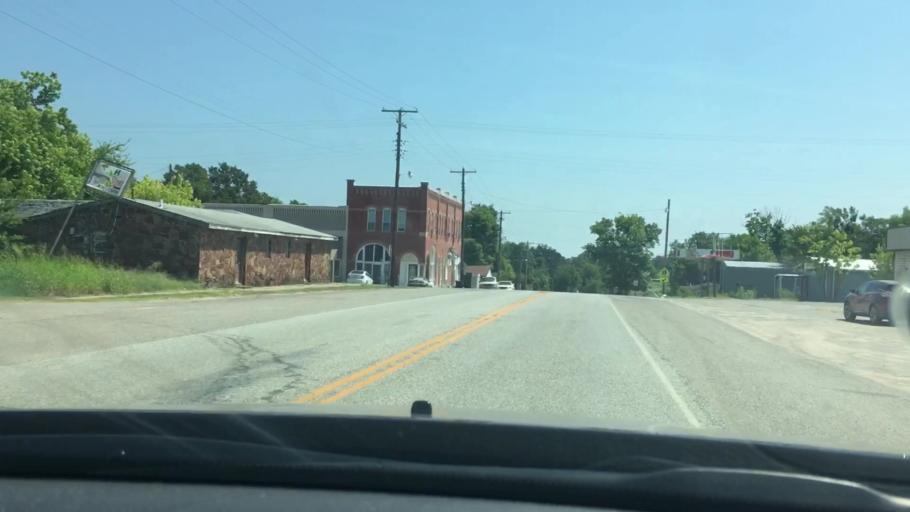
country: US
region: Oklahoma
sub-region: Johnston County
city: Tishomingo
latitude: 34.2404
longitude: -96.5507
